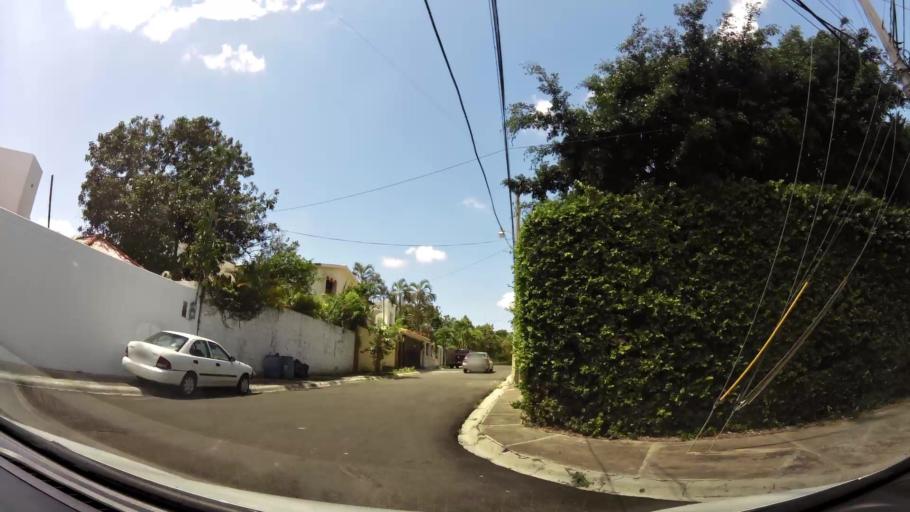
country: DO
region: Santiago
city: Santiago de los Caballeros
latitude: 19.4719
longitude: -70.6796
